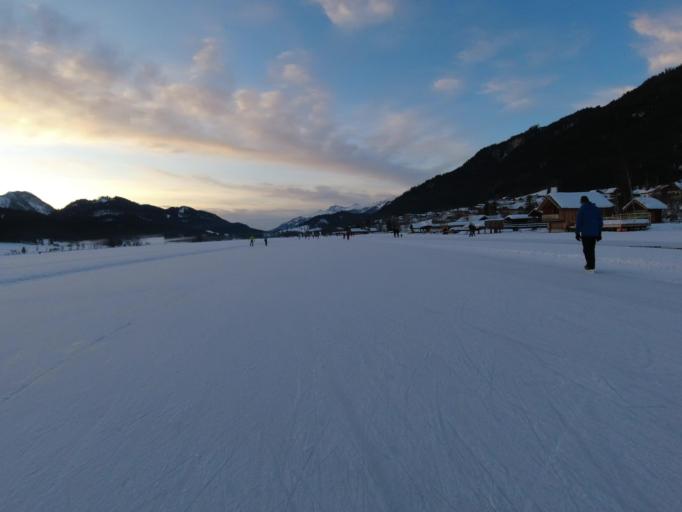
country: AT
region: Carinthia
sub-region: Politischer Bezirk Spittal an der Drau
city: Steinfeld
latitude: 46.7171
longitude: 13.2833
